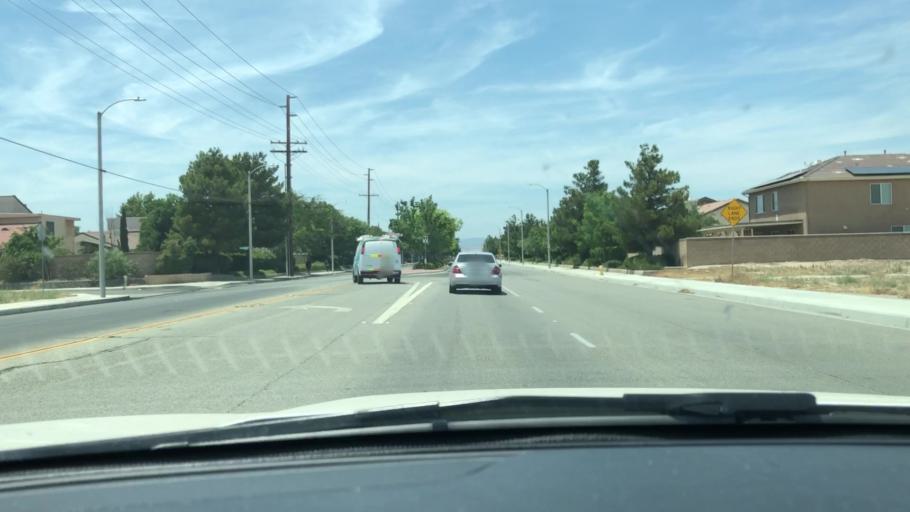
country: US
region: California
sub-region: Los Angeles County
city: Quartz Hill
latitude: 34.6894
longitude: -118.1943
